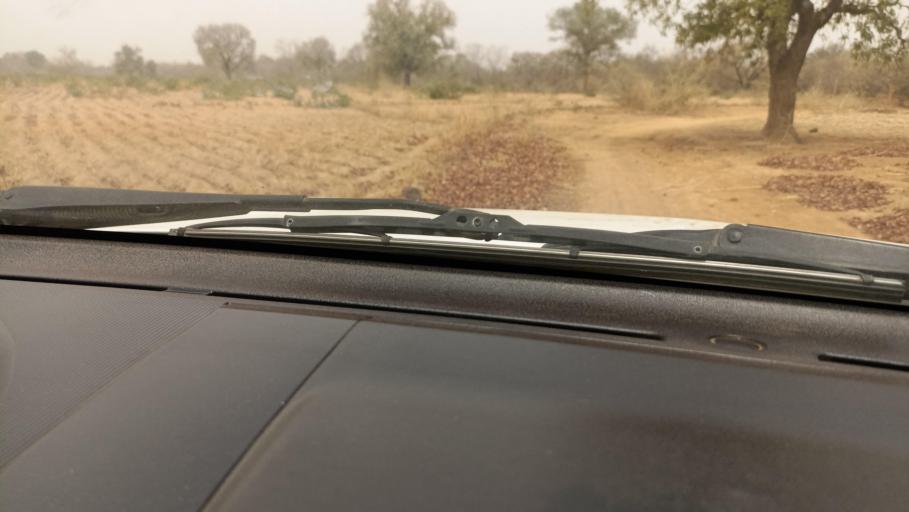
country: BF
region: Boucle du Mouhoun
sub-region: Province du Nayala
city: Toma
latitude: 12.8556
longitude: -2.8057
